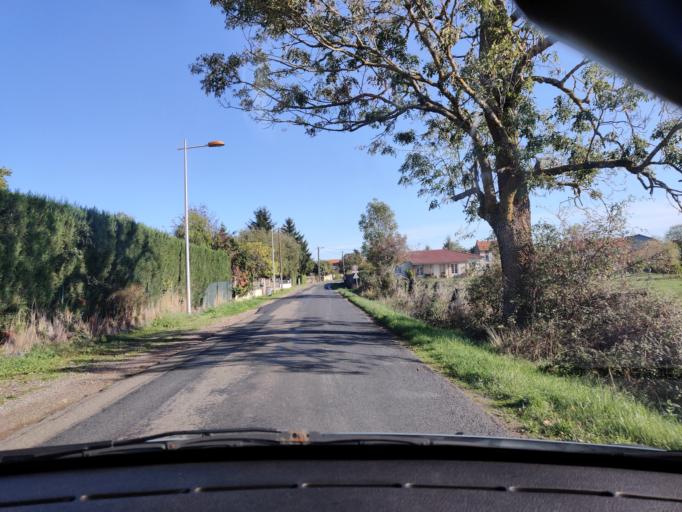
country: FR
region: Auvergne
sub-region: Departement du Puy-de-Dome
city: Combronde
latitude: 46.0372
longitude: 3.1240
